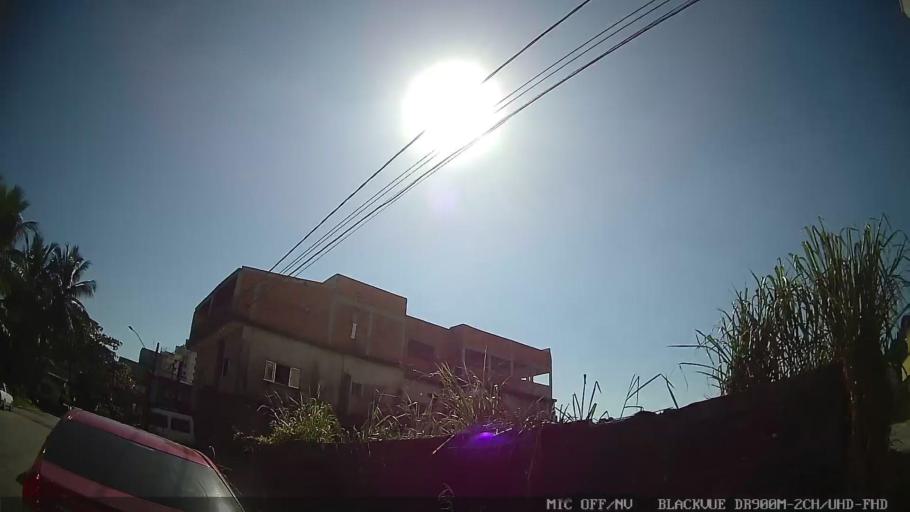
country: BR
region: Sao Paulo
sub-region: Guaruja
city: Guaruja
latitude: -23.9857
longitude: -46.2017
